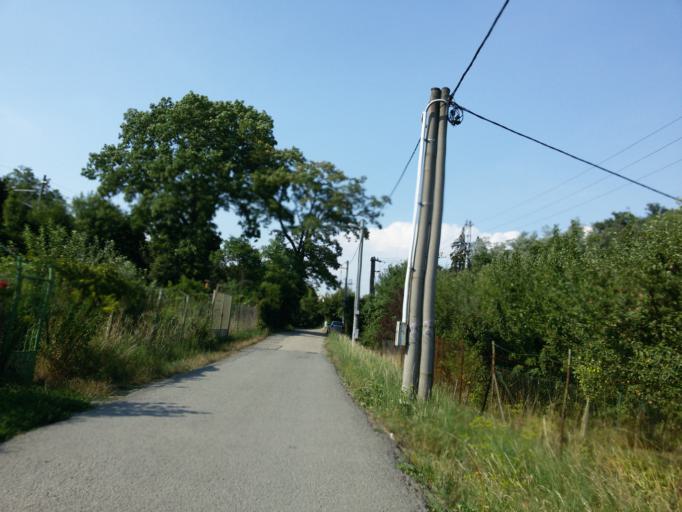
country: CZ
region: South Moravian
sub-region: Mesto Brno
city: Mokra Hora
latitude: 49.2460
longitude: 16.5900
